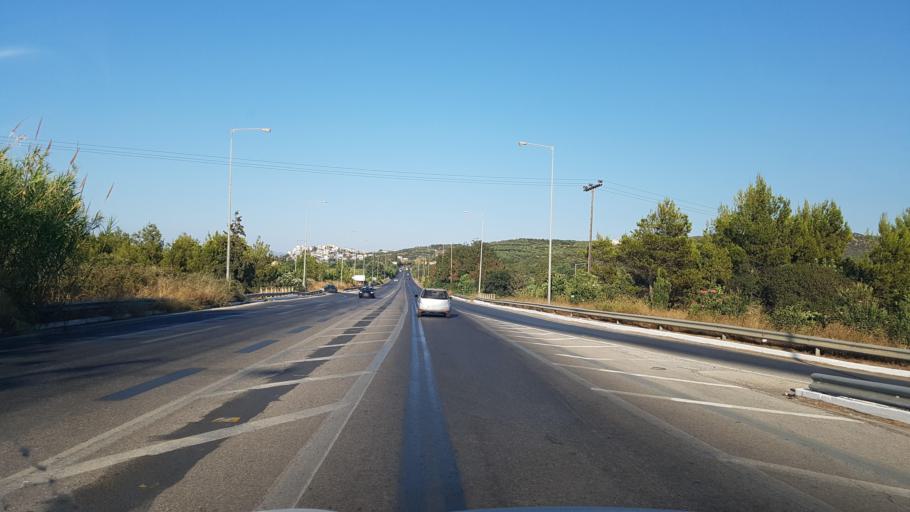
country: GR
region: Crete
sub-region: Nomos Chanias
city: Gerani
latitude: 35.5120
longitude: 23.8899
